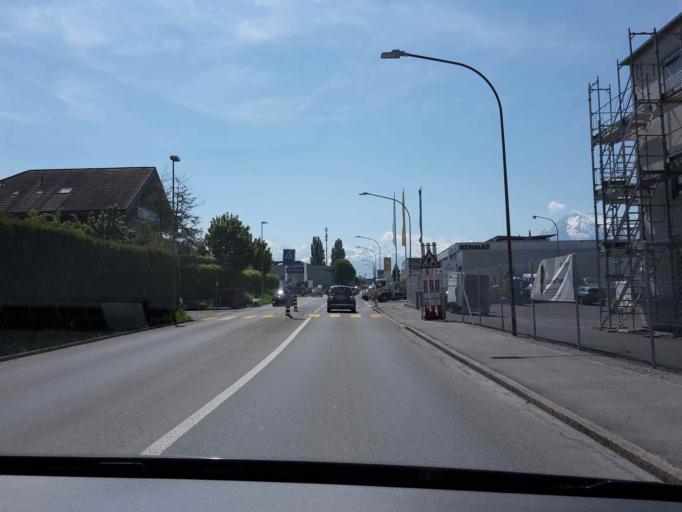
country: CH
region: Bern
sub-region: Thun District
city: Steffisburg
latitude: 46.7770
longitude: 7.6141
